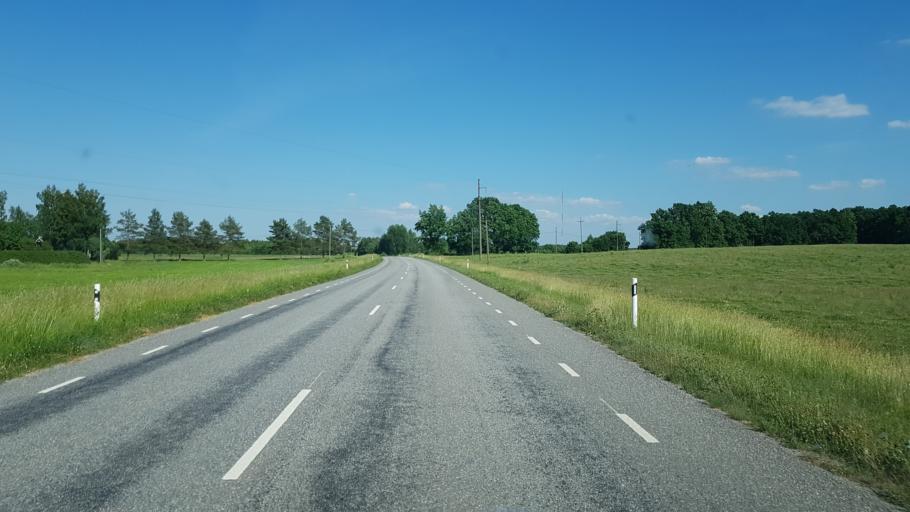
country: EE
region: Vorumaa
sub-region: Voru linn
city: Voru
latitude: 57.8560
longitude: 27.1647
